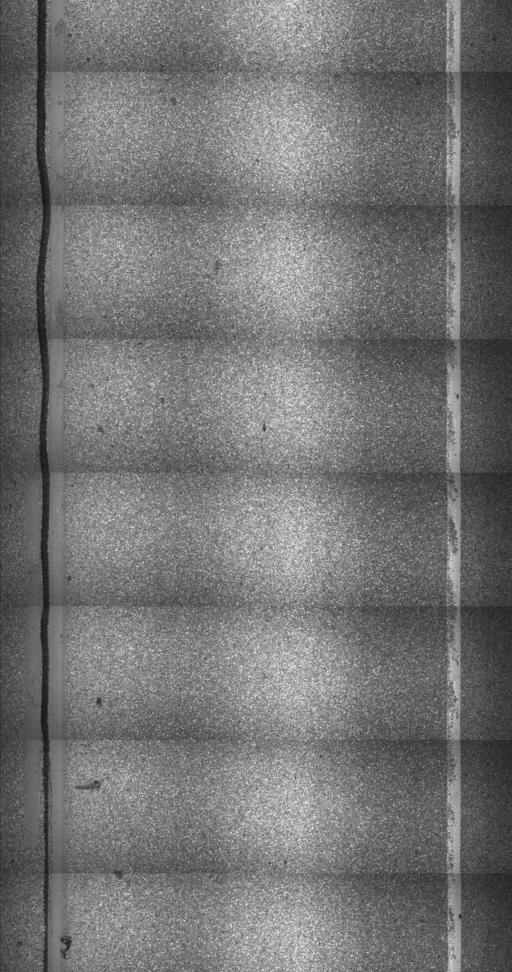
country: US
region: Vermont
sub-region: Franklin County
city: Saint Albans
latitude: 44.8523
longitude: -73.0909
